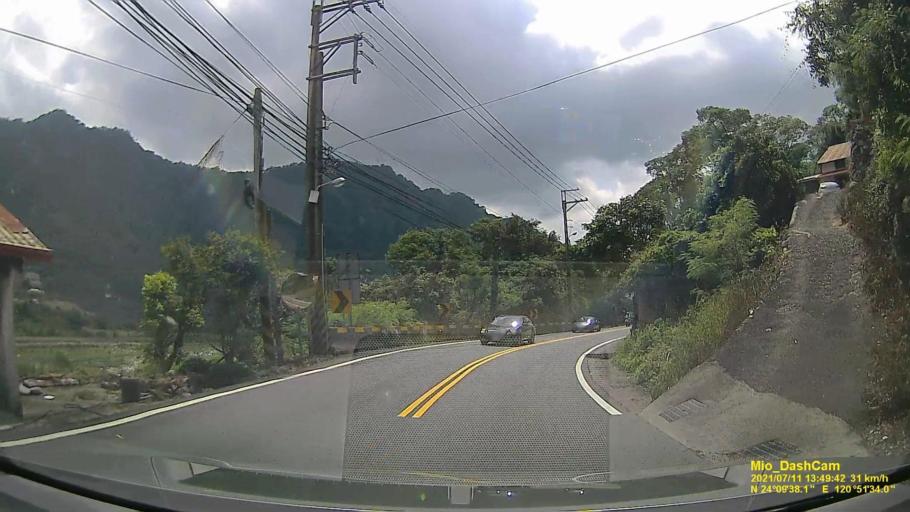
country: TW
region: Taiwan
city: Fengyuan
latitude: 24.1606
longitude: 120.8594
